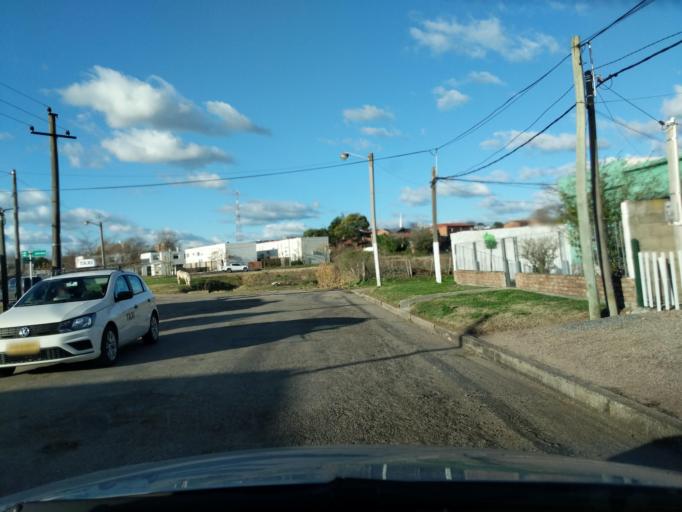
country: UY
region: Florida
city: Florida
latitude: -34.1020
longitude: -56.2241
